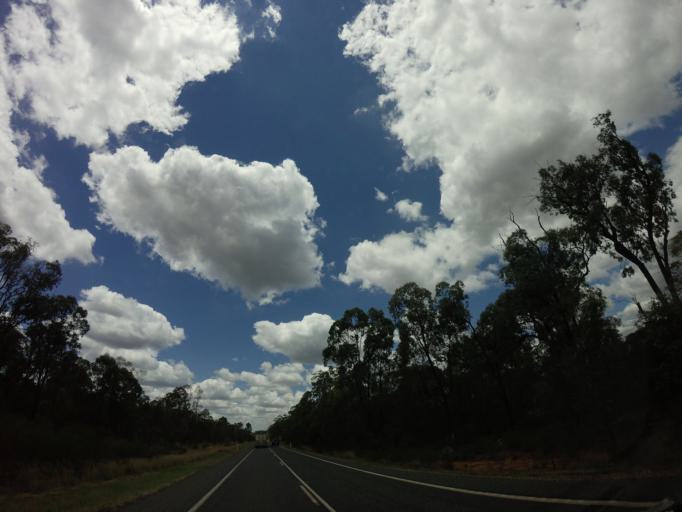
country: AU
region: Queensland
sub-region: Goondiwindi
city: Goondiwindi
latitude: -27.9997
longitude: 150.9404
